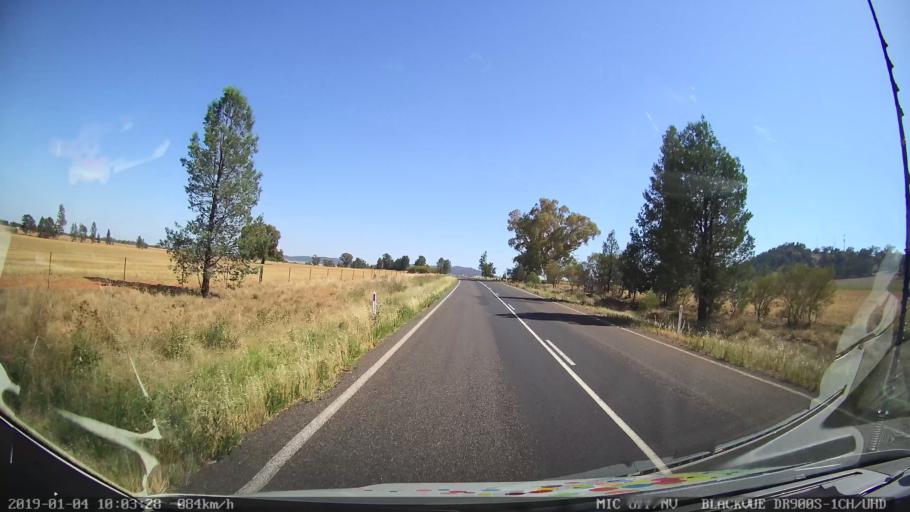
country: AU
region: New South Wales
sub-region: Cabonne
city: Canowindra
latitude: -33.4633
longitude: 148.3644
